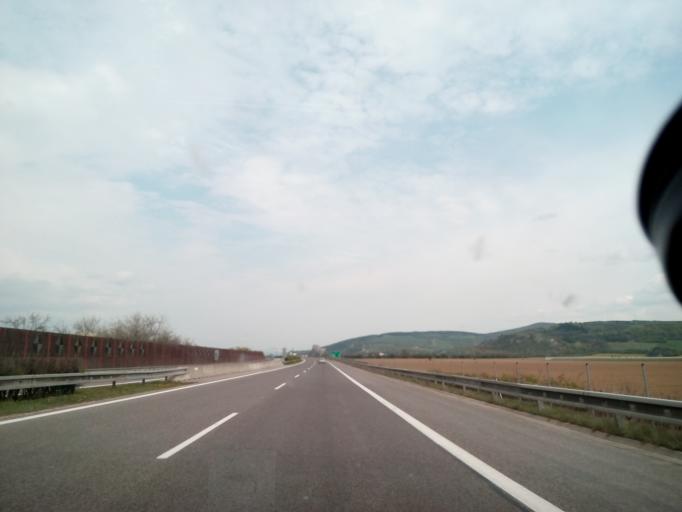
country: SK
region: Trenciansky
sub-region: Okres Nove Mesto nad Vahom
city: Nove Mesto nad Vahom
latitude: 48.7655
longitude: 17.8710
